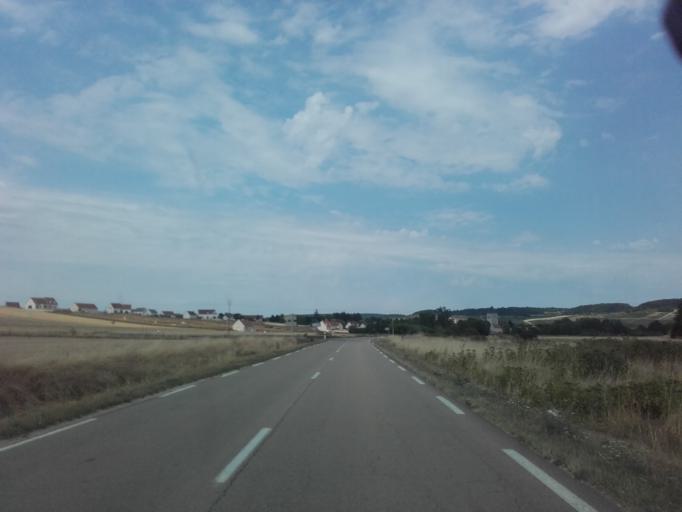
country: FR
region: Bourgogne
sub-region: Departement de l'Yonne
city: Chablis
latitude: 47.8021
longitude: 3.7983
